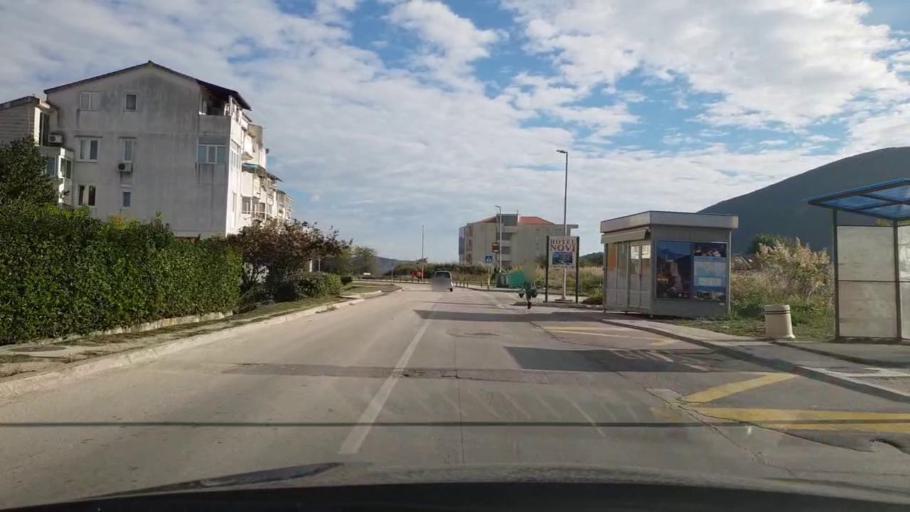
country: ME
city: Igalo
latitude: 42.4545
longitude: 18.5037
